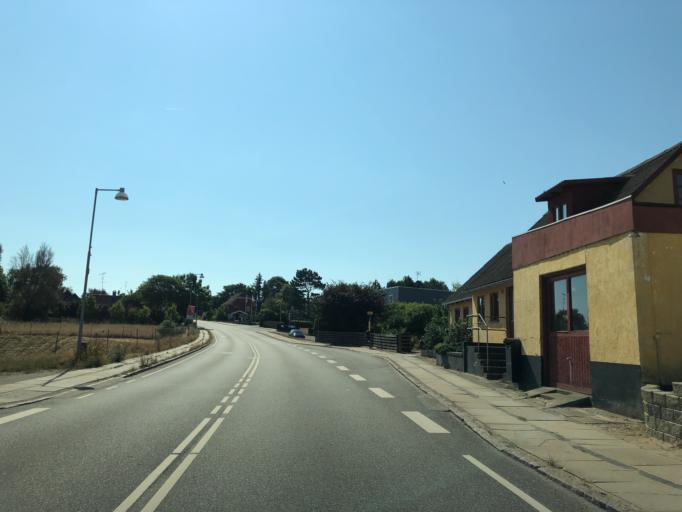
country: DK
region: Zealand
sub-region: Odsherred Kommune
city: Asnaes
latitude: 55.9661
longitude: 11.3670
